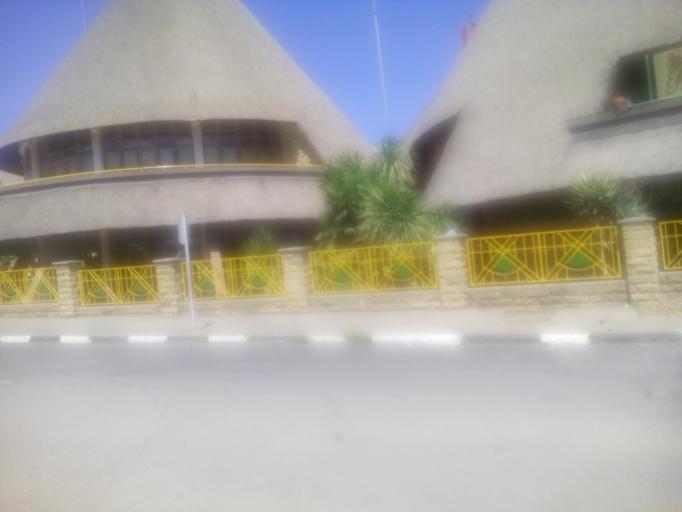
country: LS
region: Maseru
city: Maseru
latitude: -29.3130
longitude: 27.4781
